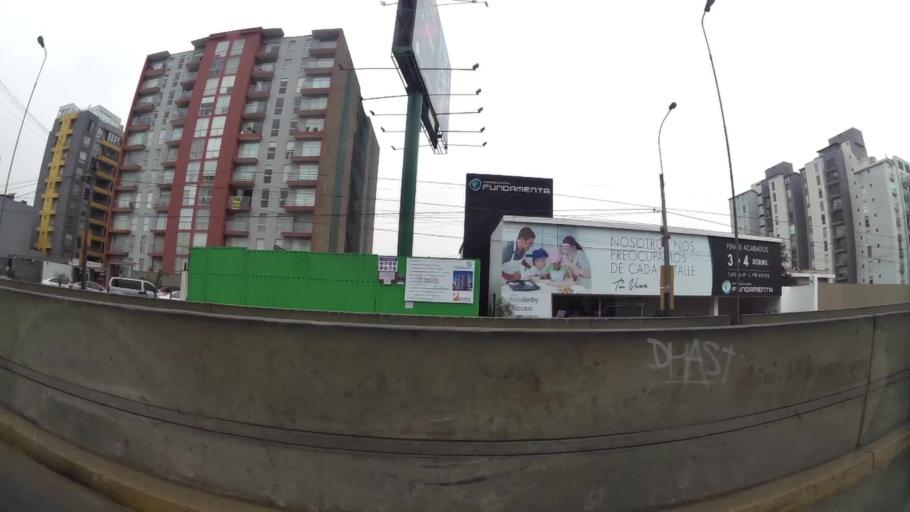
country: PE
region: Lima
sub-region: Lima
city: San Luis
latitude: -12.0986
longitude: -76.9779
